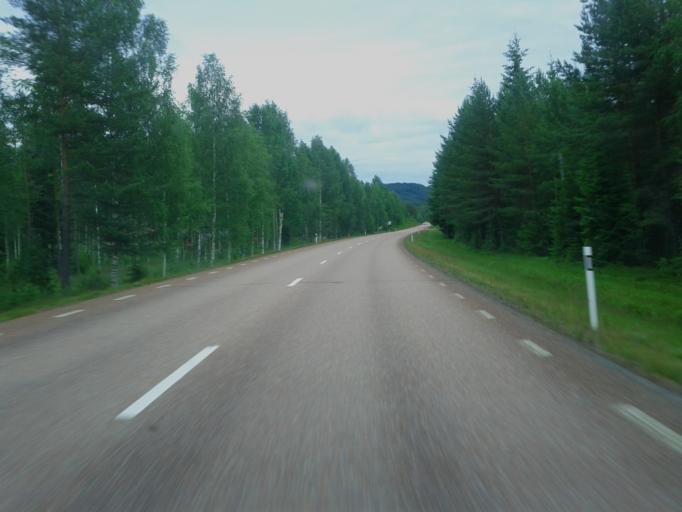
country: SE
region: Dalarna
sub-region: Alvdalens Kommun
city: AElvdalen
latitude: 61.1218
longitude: 14.2329
